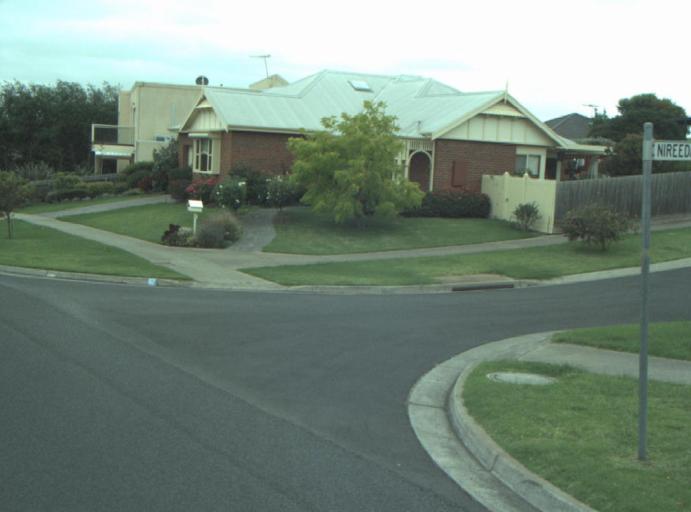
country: AU
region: Victoria
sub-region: Greater Geelong
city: Wandana Heights
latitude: -38.1766
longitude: 144.3056
